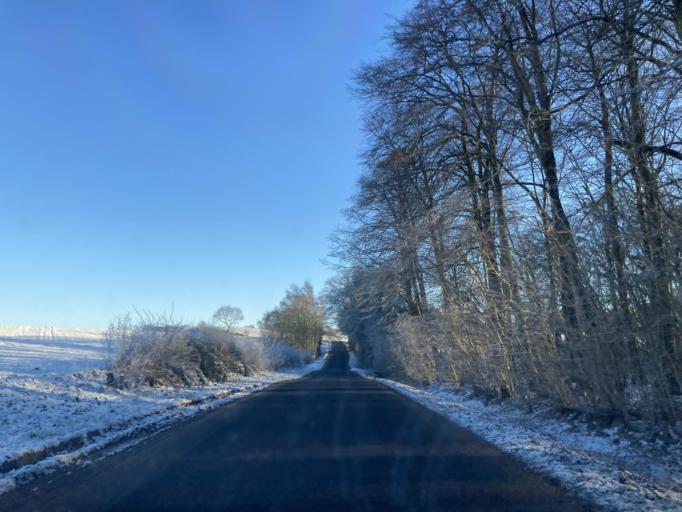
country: DK
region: South Denmark
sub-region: Svendborg Kommune
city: Svendborg
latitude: 55.1283
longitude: 10.5856
